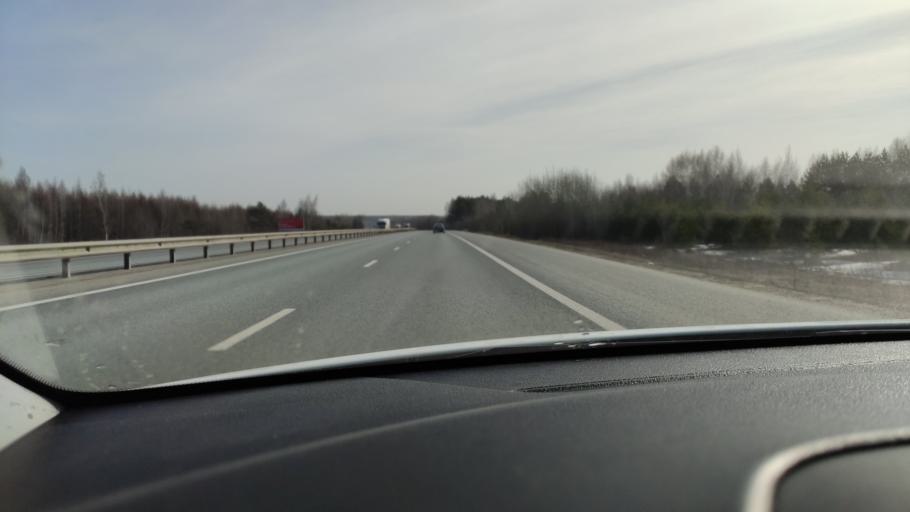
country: RU
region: Tatarstan
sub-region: Gorod Kazan'
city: Kazan
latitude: 55.9135
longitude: 49.1000
